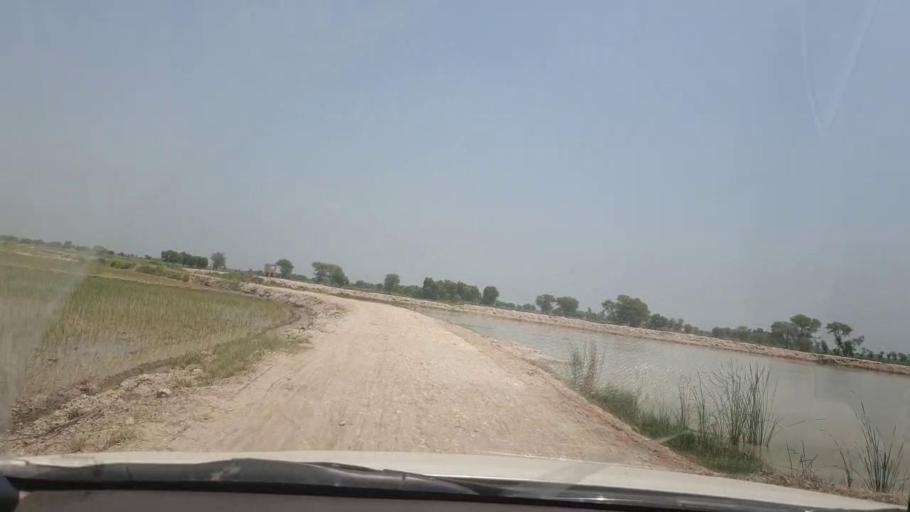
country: PK
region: Sindh
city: Lakhi
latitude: 27.8650
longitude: 68.7187
